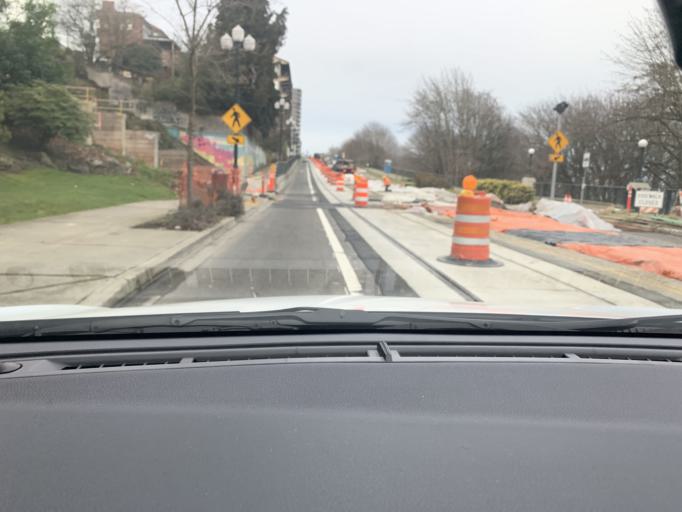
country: US
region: Washington
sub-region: Pierce County
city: Tacoma
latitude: 47.2625
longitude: -122.4439
